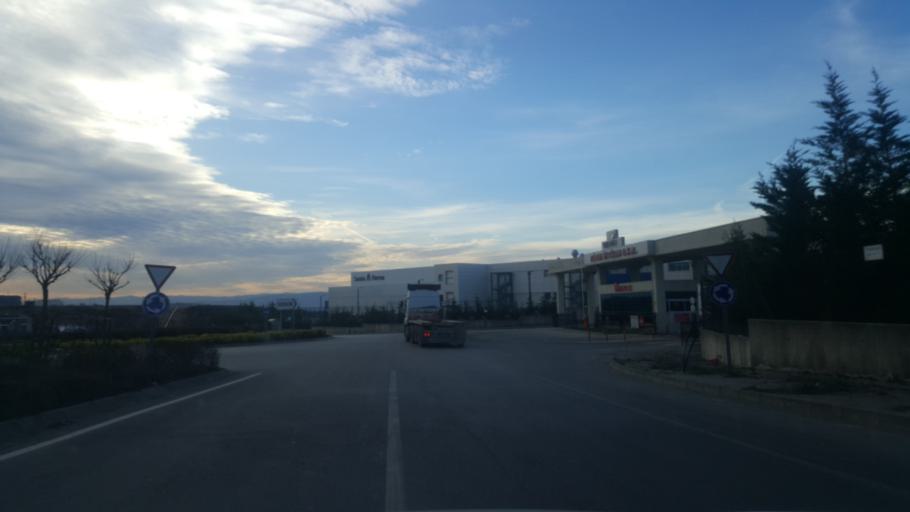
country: TR
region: Kocaeli
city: Tavsancil
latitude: 40.8195
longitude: 29.5618
